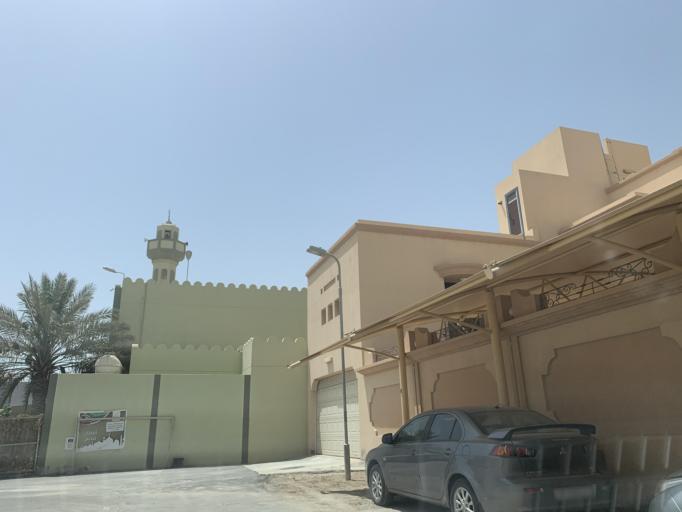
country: BH
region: Northern
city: Madinat `Isa
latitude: 26.1581
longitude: 50.5809
